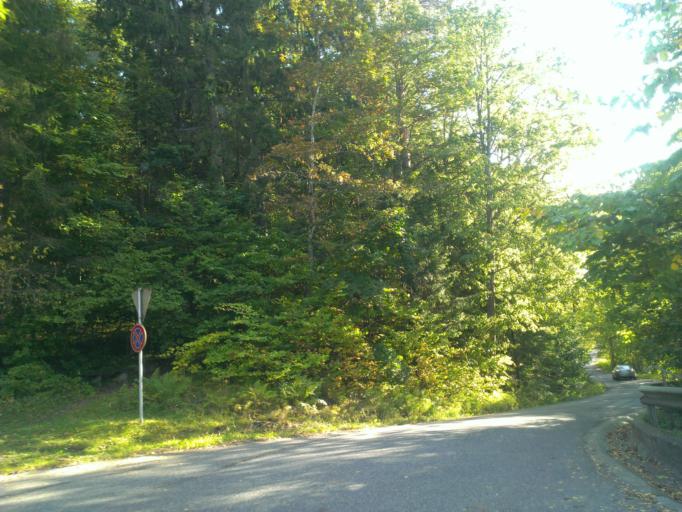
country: LV
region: Sigulda
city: Sigulda
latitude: 57.1653
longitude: 24.8420
